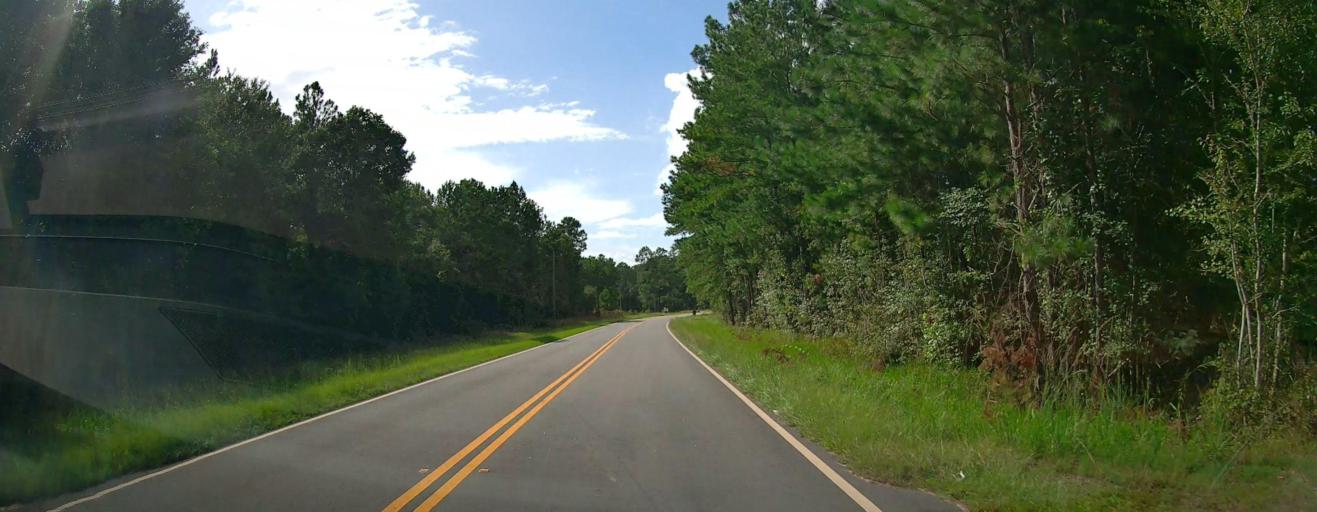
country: US
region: Georgia
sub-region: Coffee County
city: Douglas
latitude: 31.4492
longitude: -82.8785
